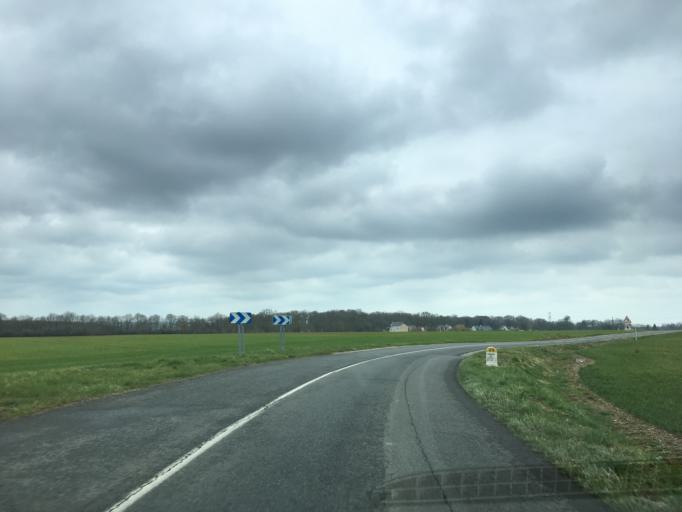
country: FR
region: Centre
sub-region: Departement d'Indre-et-Loire
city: Parcay-Meslay
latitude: 47.4680
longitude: 0.7370
